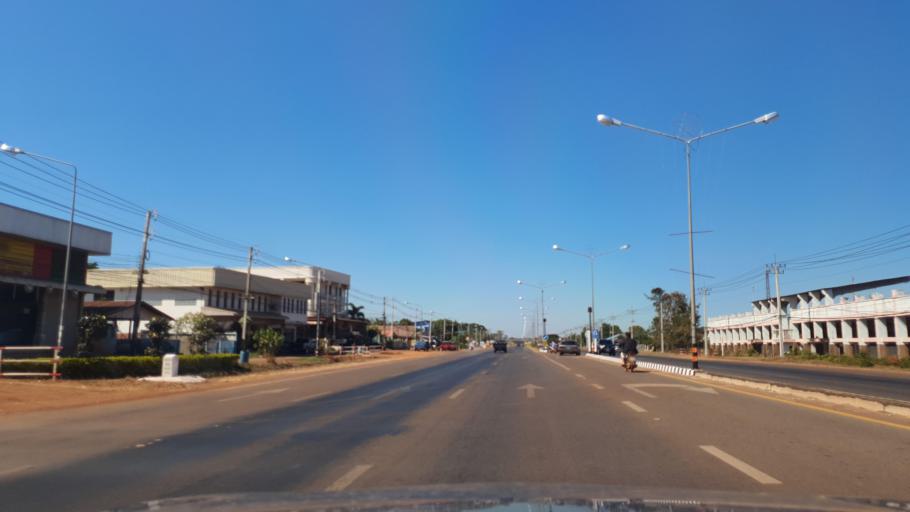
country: TH
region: Sakon Nakhon
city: Sakon Nakhon
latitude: 17.2562
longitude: 104.1811
